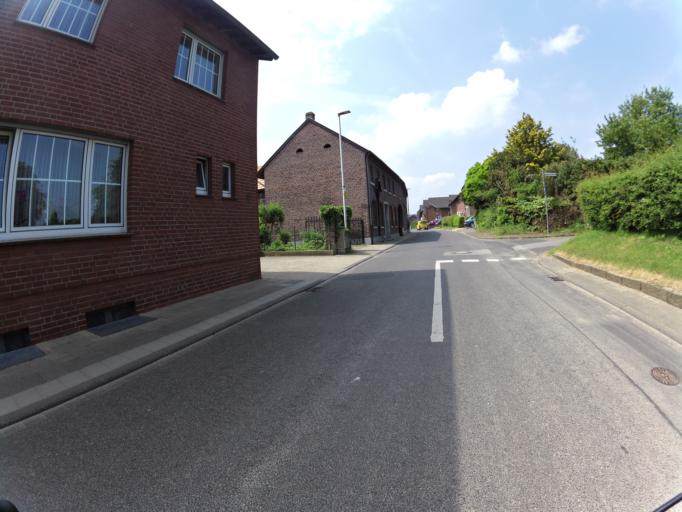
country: DE
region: North Rhine-Westphalia
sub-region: Regierungsbezirk Koln
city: Gangelt
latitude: 50.9875
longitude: 6.0322
